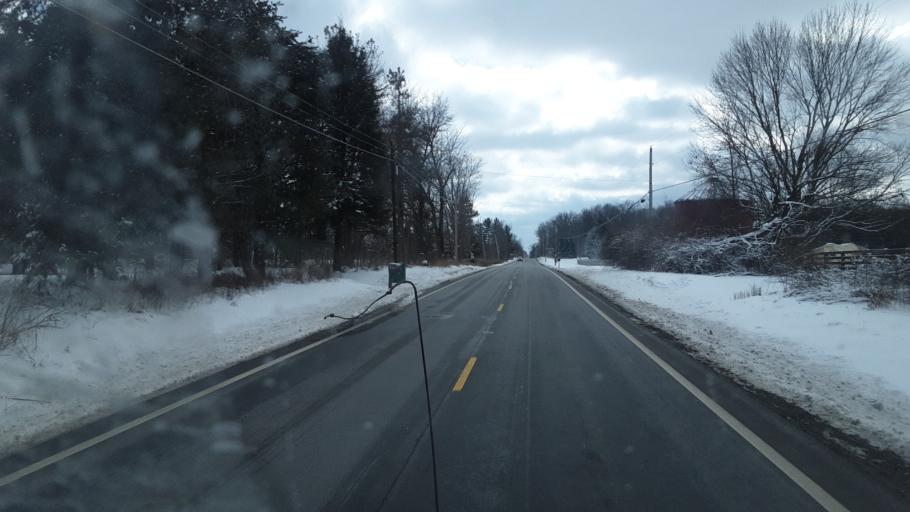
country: US
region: Ohio
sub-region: Franklin County
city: New Albany
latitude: 40.1555
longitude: -82.8082
